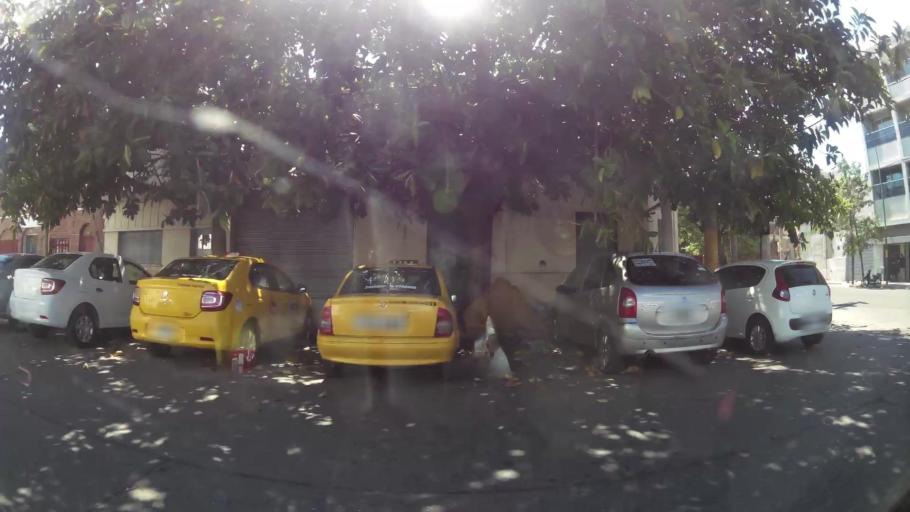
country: AR
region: Cordoba
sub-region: Departamento de Capital
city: Cordoba
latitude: -31.4013
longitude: -64.1761
